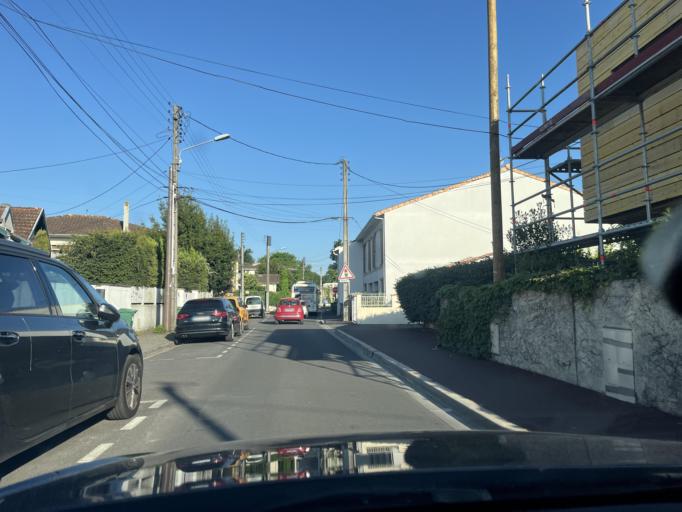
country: FR
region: Aquitaine
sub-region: Departement de la Gironde
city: Merignac
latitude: 44.8347
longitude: -0.6246
